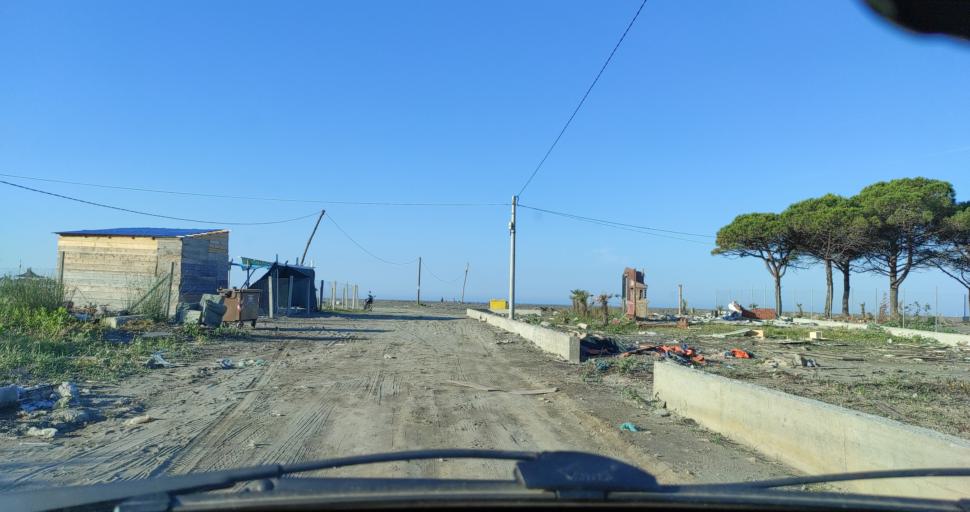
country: AL
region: Shkoder
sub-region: Rrethi i Shkodres
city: Velipoje
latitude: 41.8611
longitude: 19.4358
